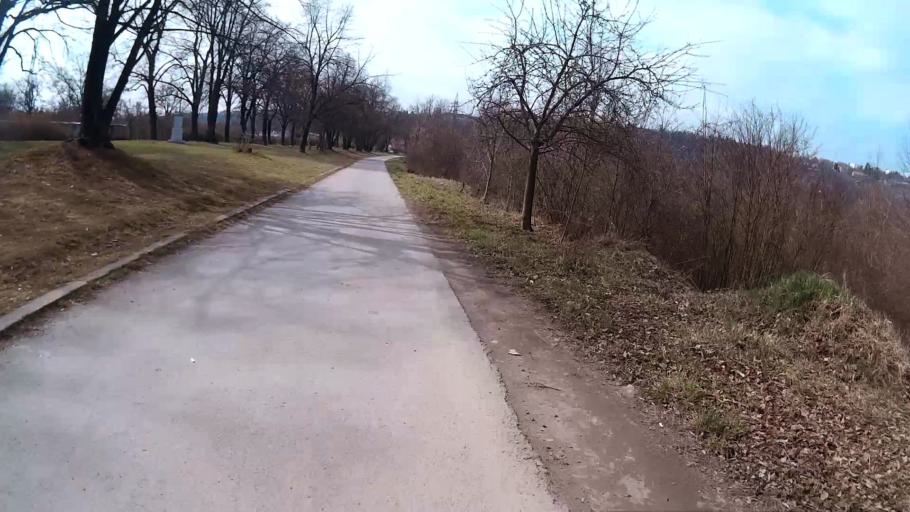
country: CZ
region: South Moravian
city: Bilovice nad Svitavou
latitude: 49.2254
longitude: 16.6439
